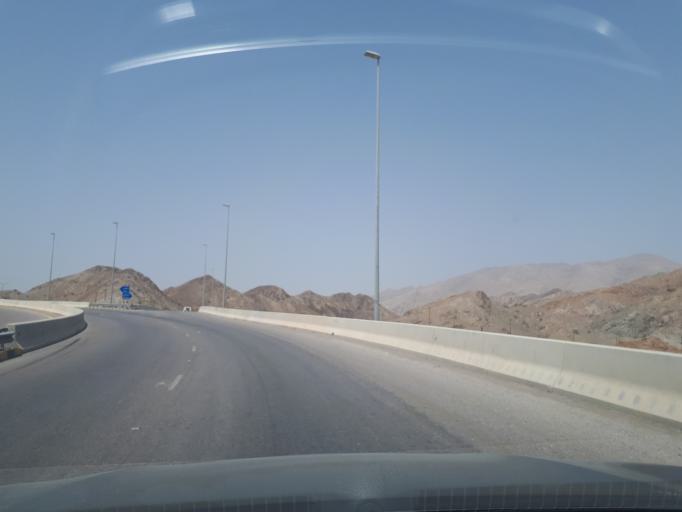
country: OM
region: Muhafazat ad Dakhiliyah
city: Bidbid
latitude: 23.4145
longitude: 58.1032
